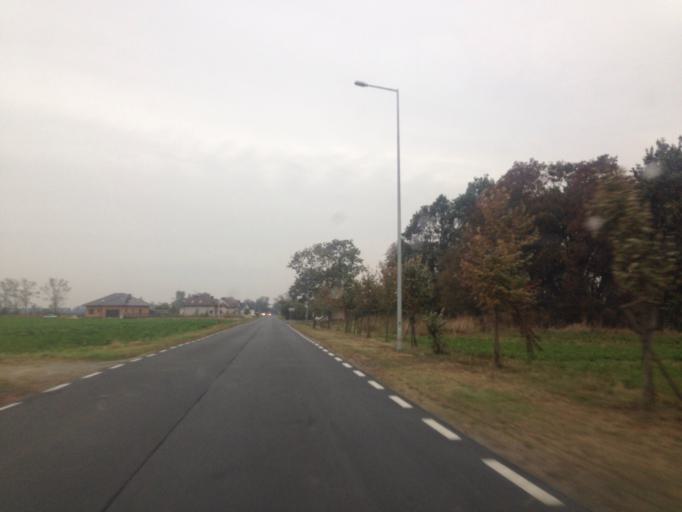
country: PL
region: Greater Poland Voivodeship
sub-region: Powiat poznanski
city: Kleszczewo
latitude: 52.3580
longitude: 17.1253
